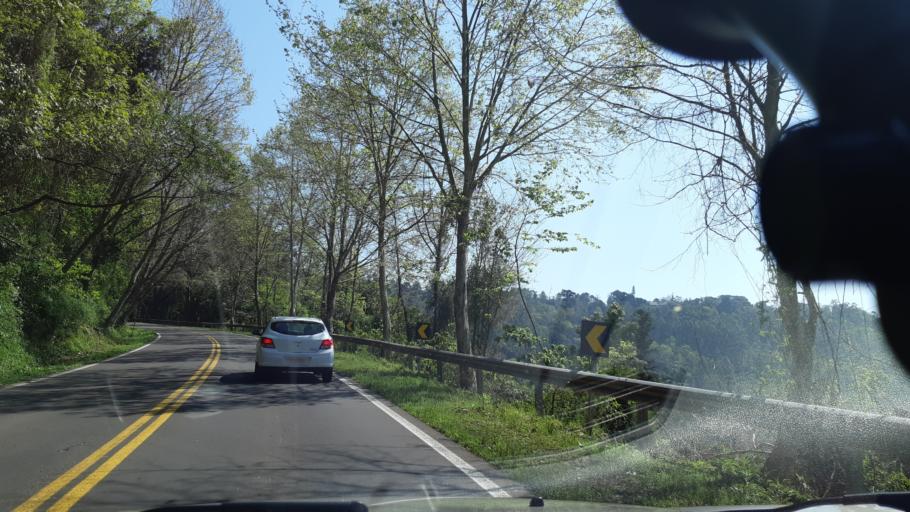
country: BR
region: Rio Grande do Sul
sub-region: Nova Petropolis
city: Nova Petropolis
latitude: -29.4030
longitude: -51.1247
